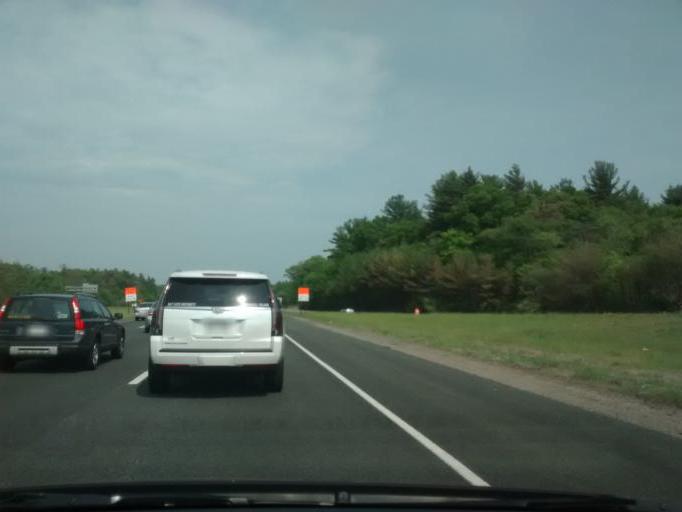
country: US
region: Massachusetts
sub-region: Bristol County
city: Raynham
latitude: 41.9586
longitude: -71.0664
